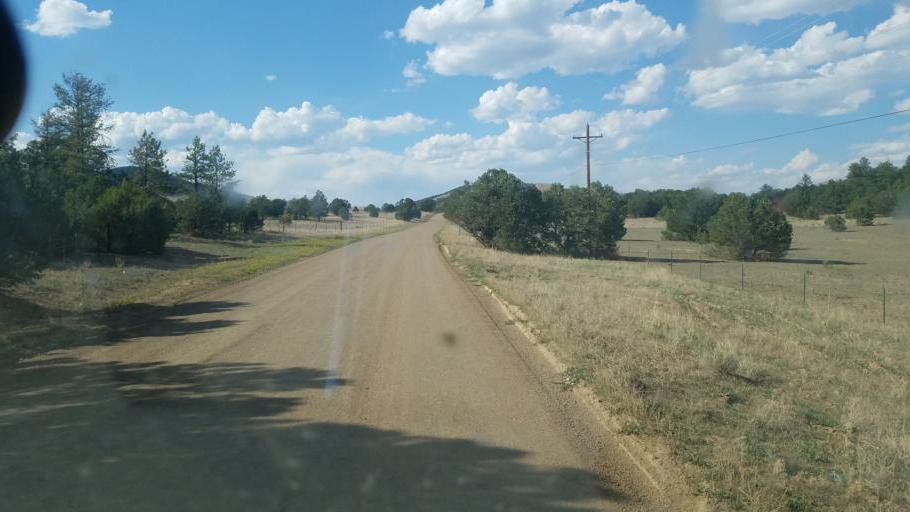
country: US
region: Colorado
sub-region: Custer County
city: Westcliffe
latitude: 38.3025
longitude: -105.4865
